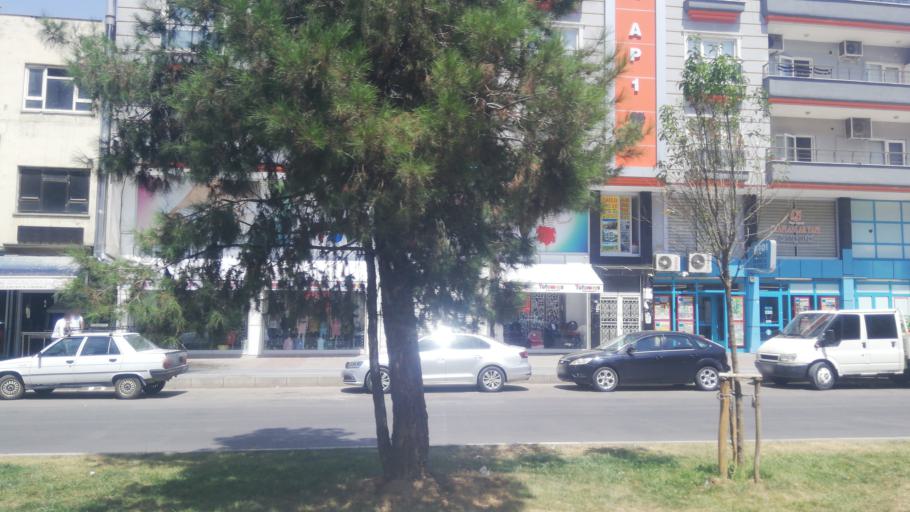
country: TR
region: Mardin
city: Midyat
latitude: 37.4220
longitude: 41.3475
